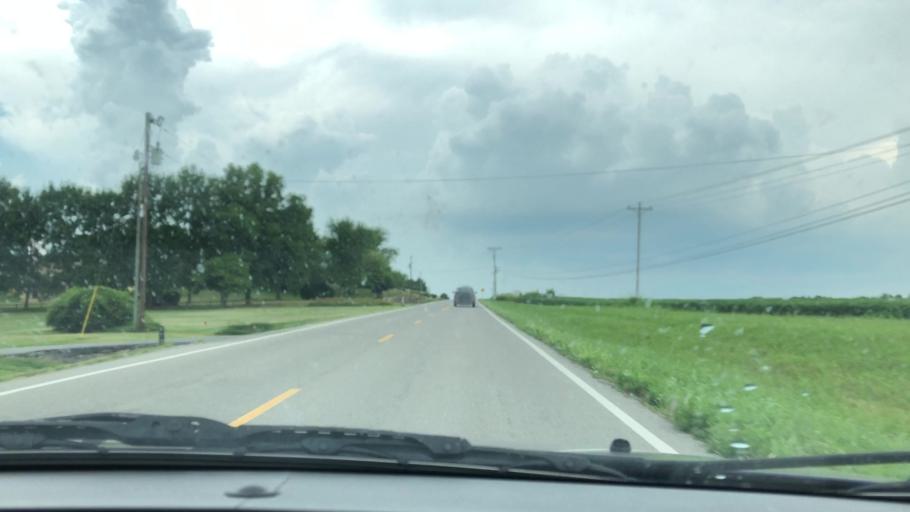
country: US
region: Tennessee
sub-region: Maury County
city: Columbia
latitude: 35.7078
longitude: -87.0155
